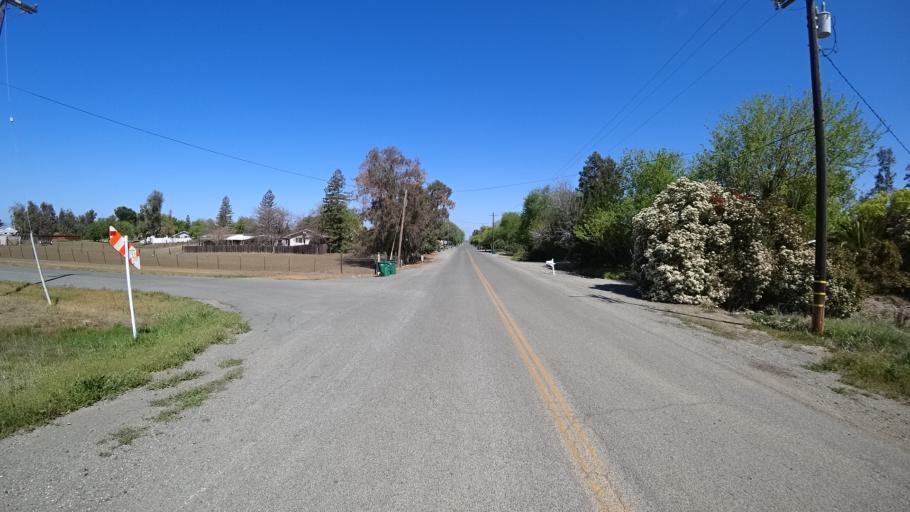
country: US
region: California
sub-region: Glenn County
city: Willows
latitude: 39.5316
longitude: -122.2074
